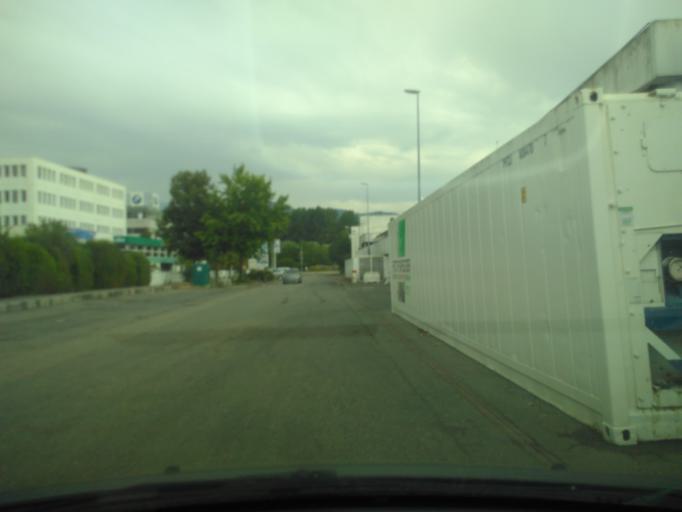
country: FR
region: Rhone-Alpes
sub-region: Departement de l'Isere
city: Corenc
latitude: 45.2039
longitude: 5.7648
